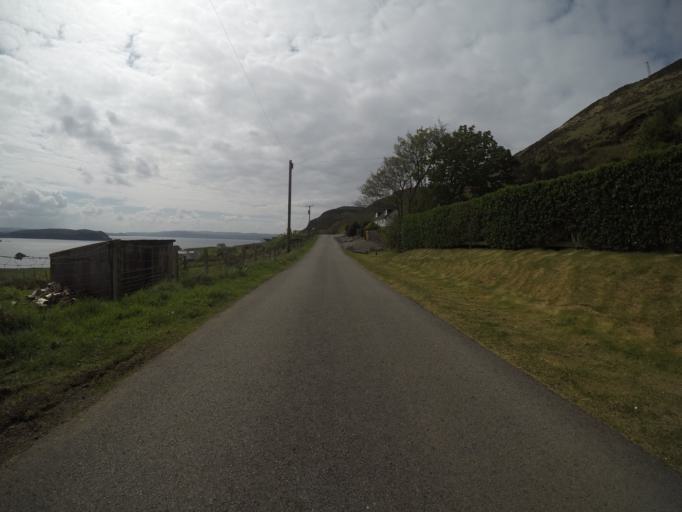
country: GB
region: Scotland
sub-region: Highland
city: Portree
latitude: 57.5893
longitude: -6.3803
